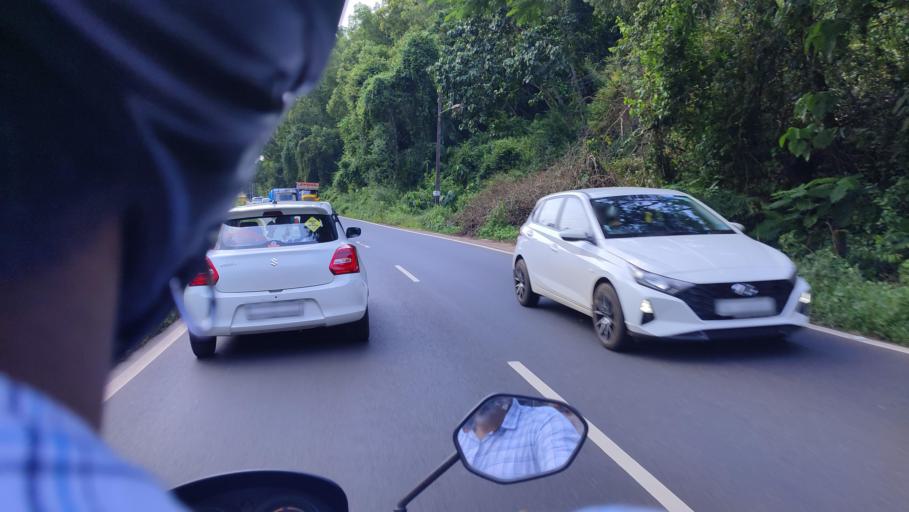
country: IN
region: Kerala
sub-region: Kasaragod District
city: Nileshwar
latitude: 12.2314
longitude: 75.1544
